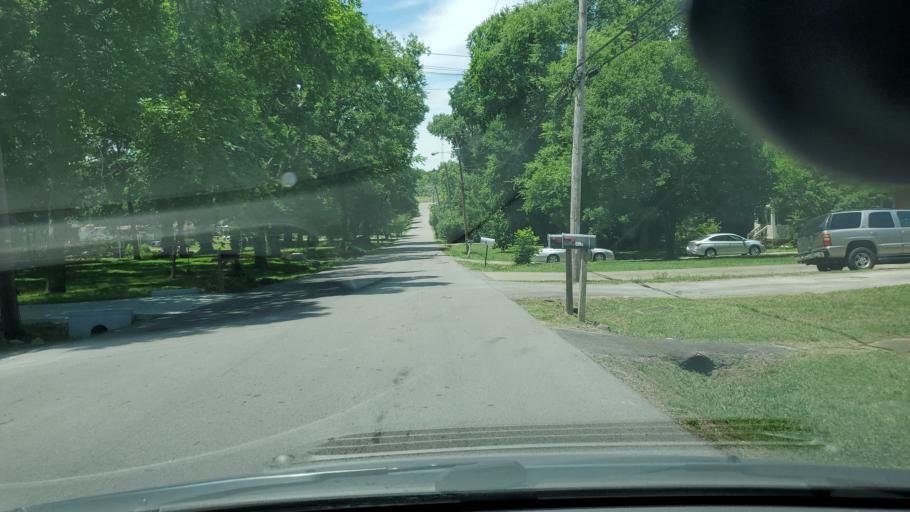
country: US
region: Tennessee
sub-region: Davidson County
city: Nashville
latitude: 36.2142
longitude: -86.7587
